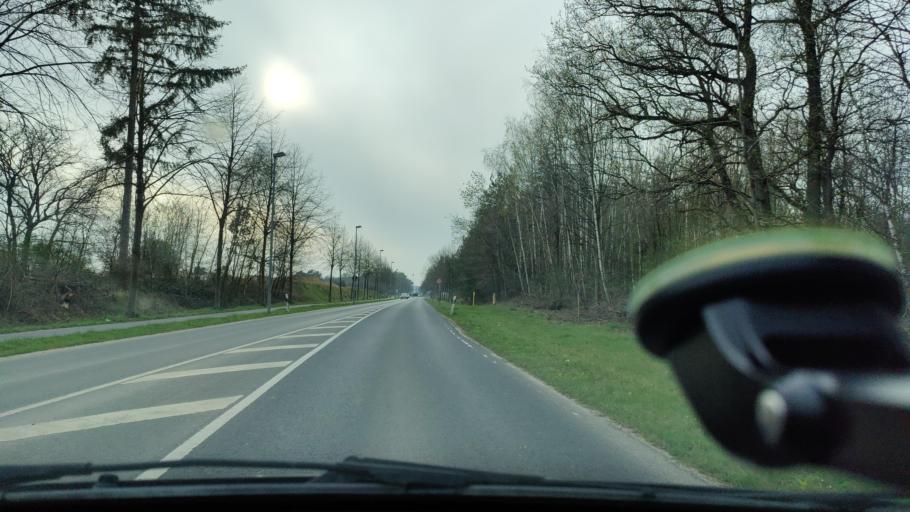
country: DE
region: North Rhine-Westphalia
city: Huckelhoven
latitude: 51.1198
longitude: 6.2219
